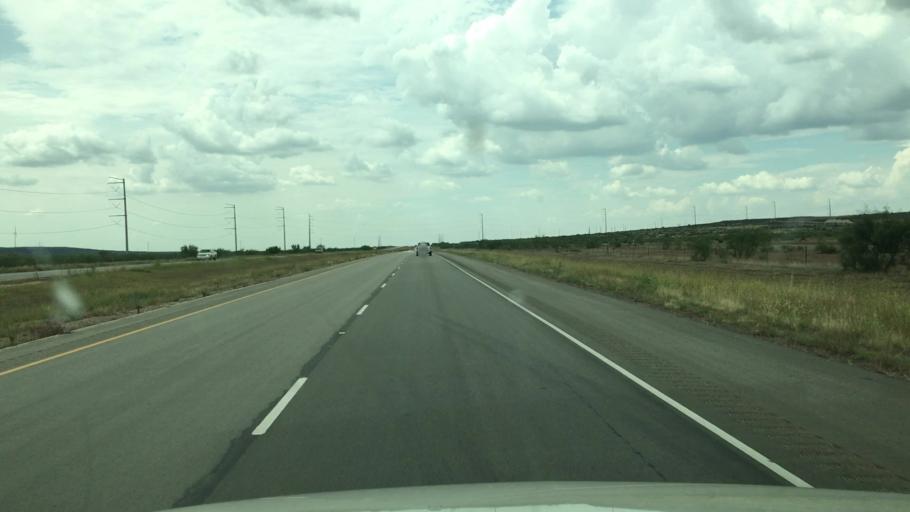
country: US
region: Texas
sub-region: Glasscock County
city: Garden City
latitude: 31.9809
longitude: -101.2552
